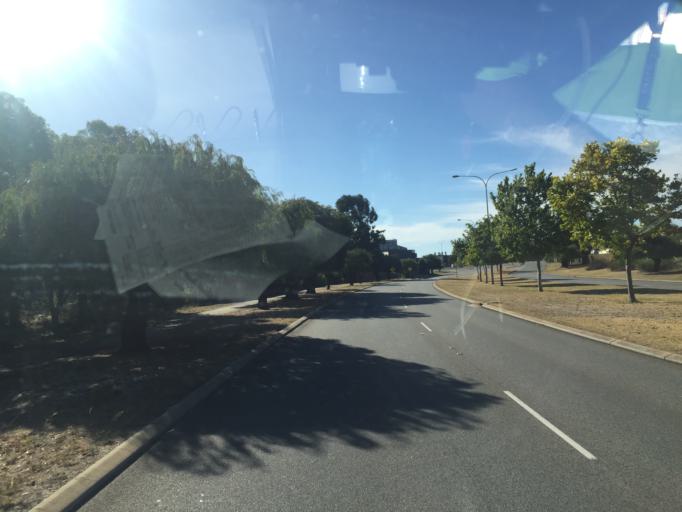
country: AU
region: Western Australia
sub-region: Canning
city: Queens Park
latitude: -31.9950
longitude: 115.9467
